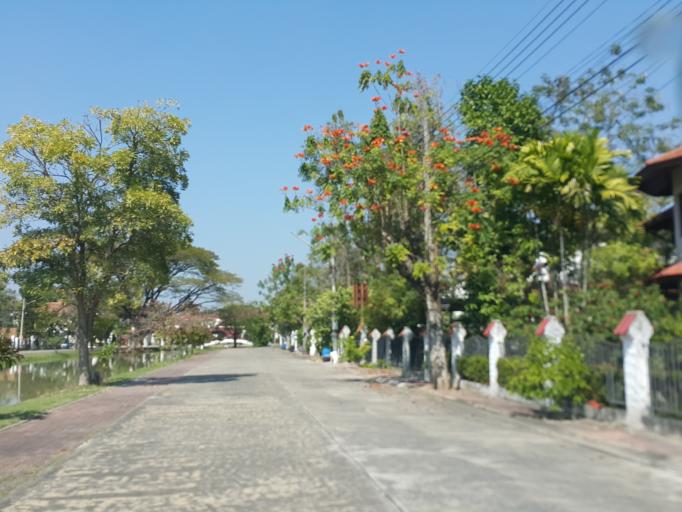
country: TH
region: Chiang Mai
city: Saraphi
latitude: 18.7566
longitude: 99.0250
